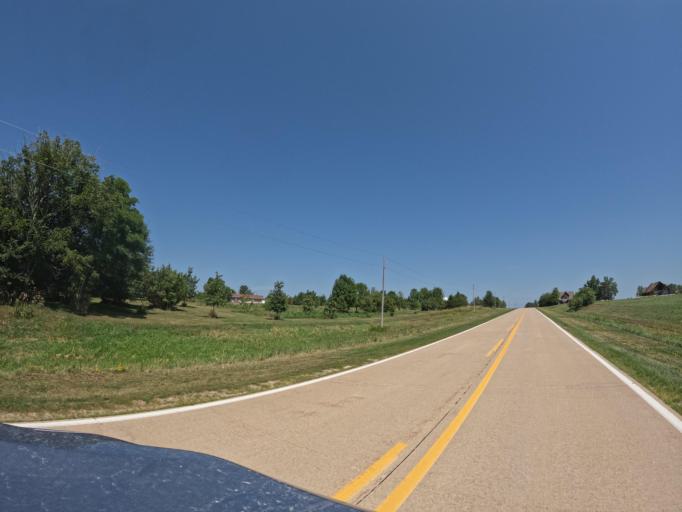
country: US
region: Iowa
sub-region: Henry County
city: Mount Pleasant
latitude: 40.8829
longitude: -91.5603
